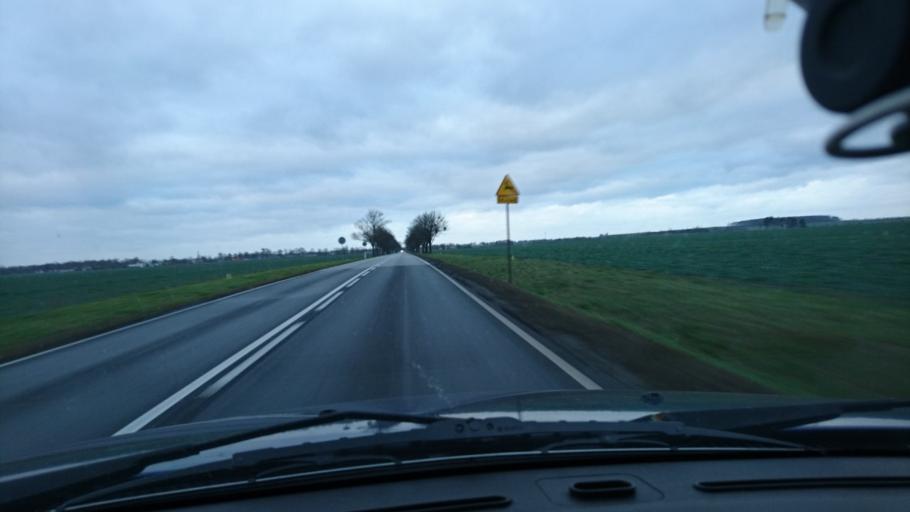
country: PL
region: Opole Voivodeship
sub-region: Powiat kluczborski
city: Byczyna
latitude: 51.0707
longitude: 18.2034
